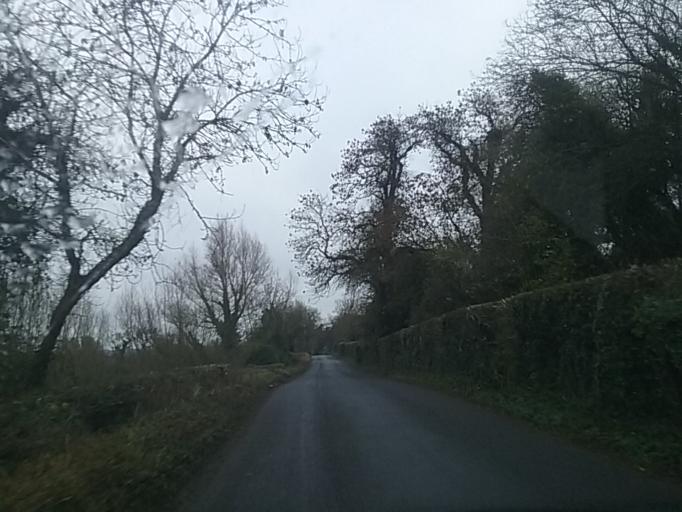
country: IE
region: Leinster
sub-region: An Mhi
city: Duleek
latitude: 53.6855
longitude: -6.4690
